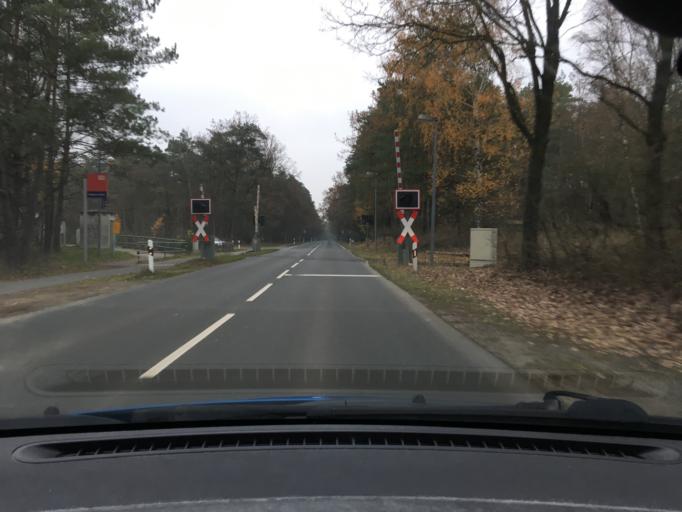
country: DE
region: Lower Saxony
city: Soltau
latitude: 53.0006
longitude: 9.8605
